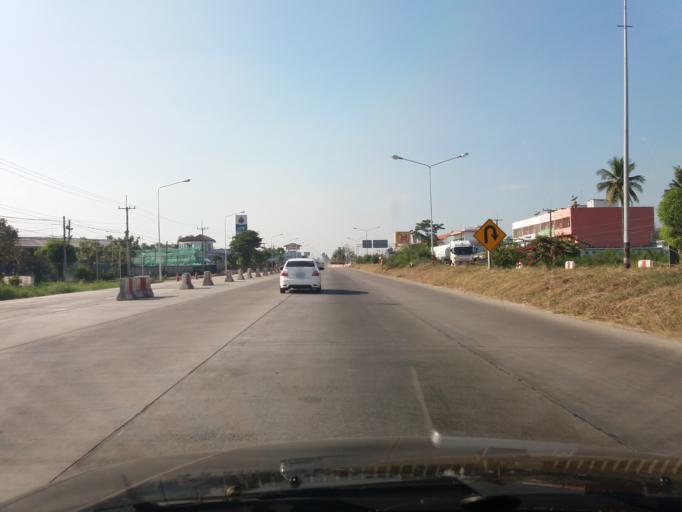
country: TH
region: Nakhon Sawan
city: Kao Liao
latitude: 15.7670
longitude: 99.9883
